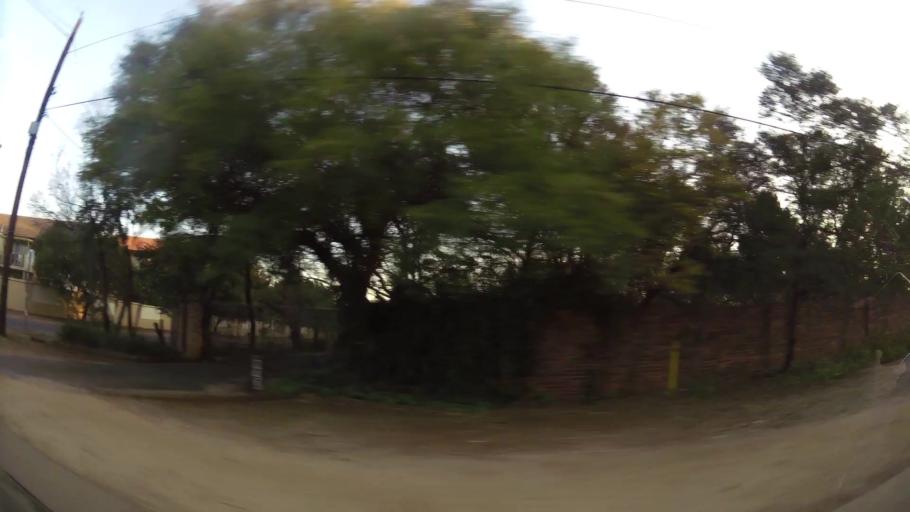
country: ZA
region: Gauteng
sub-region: City of Tshwane Metropolitan Municipality
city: Centurion
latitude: -25.8416
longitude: 28.1945
